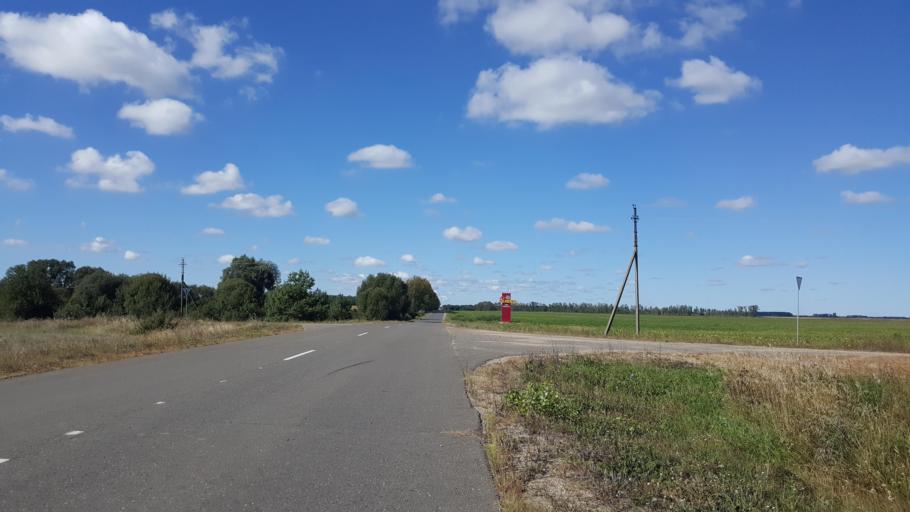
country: BY
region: Brest
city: Charnawchytsy
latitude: 52.3735
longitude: 23.5906
